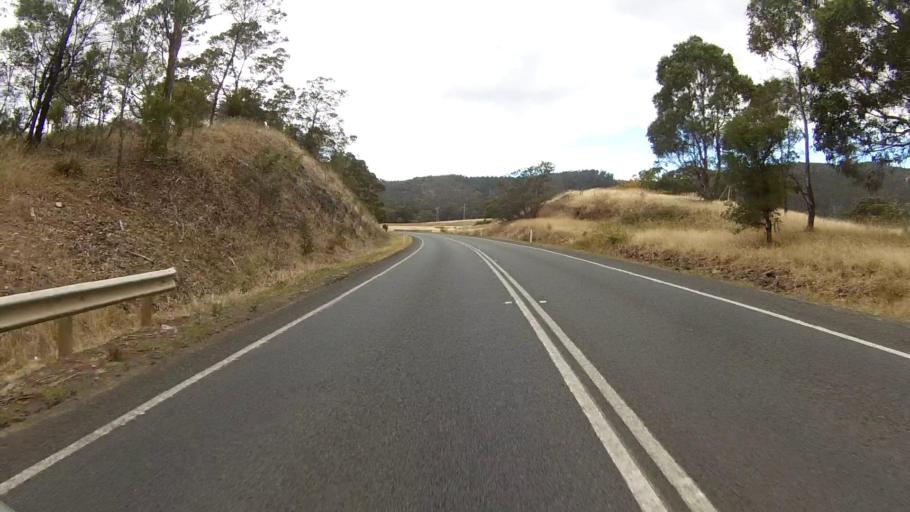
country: AU
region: Tasmania
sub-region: Sorell
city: Sorell
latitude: -42.7023
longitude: 147.5221
